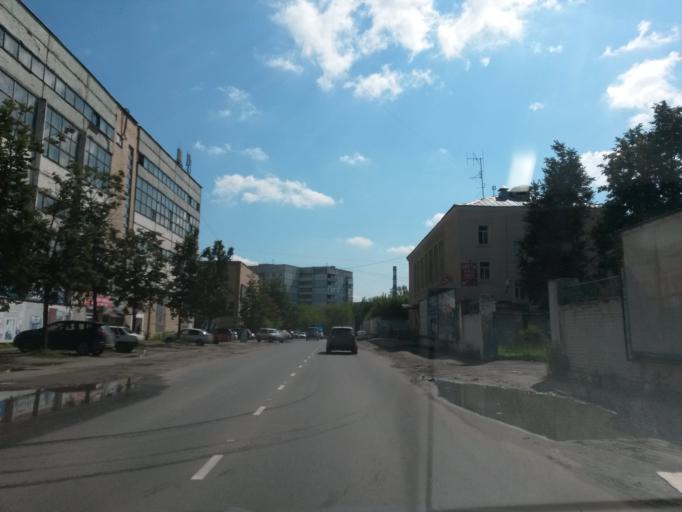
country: RU
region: Ivanovo
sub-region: Gorod Ivanovo
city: Ivanovo
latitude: 57.0095
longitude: 40.9547
